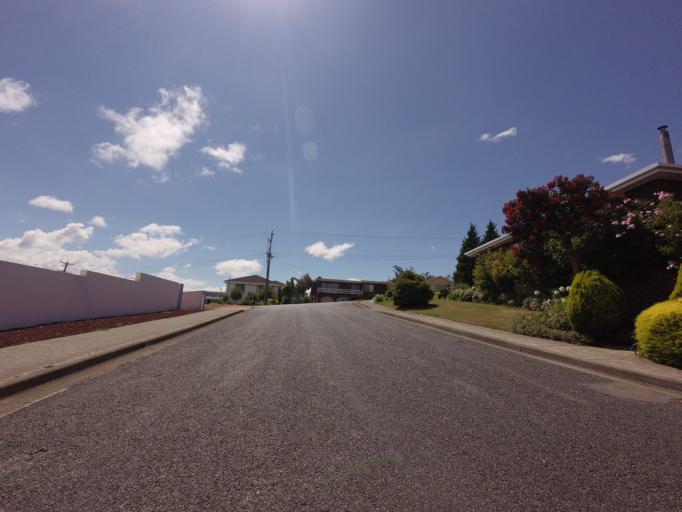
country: AU
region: Tasmania
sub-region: Clarence
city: Howrah
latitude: -42.9182
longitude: 147.4123
